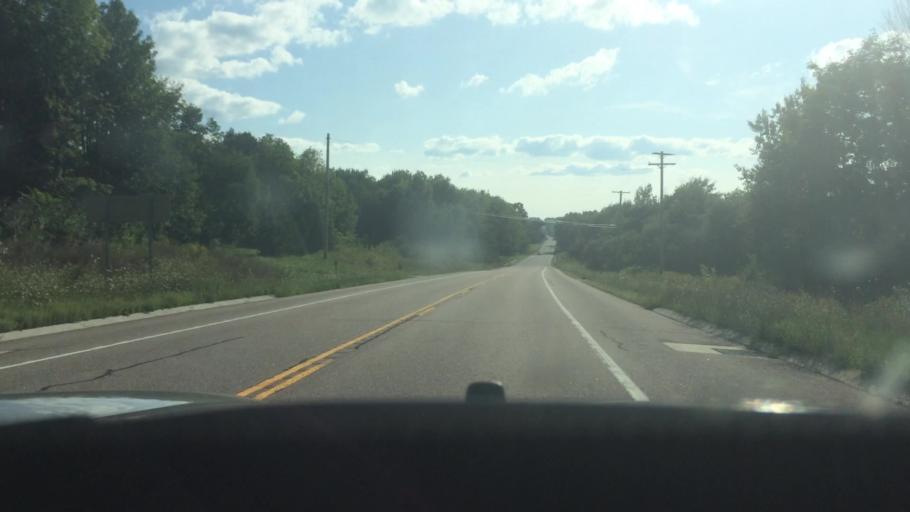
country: US
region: New York
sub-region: Franklin County
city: Malone
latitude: 44.7481
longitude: -74.5648
